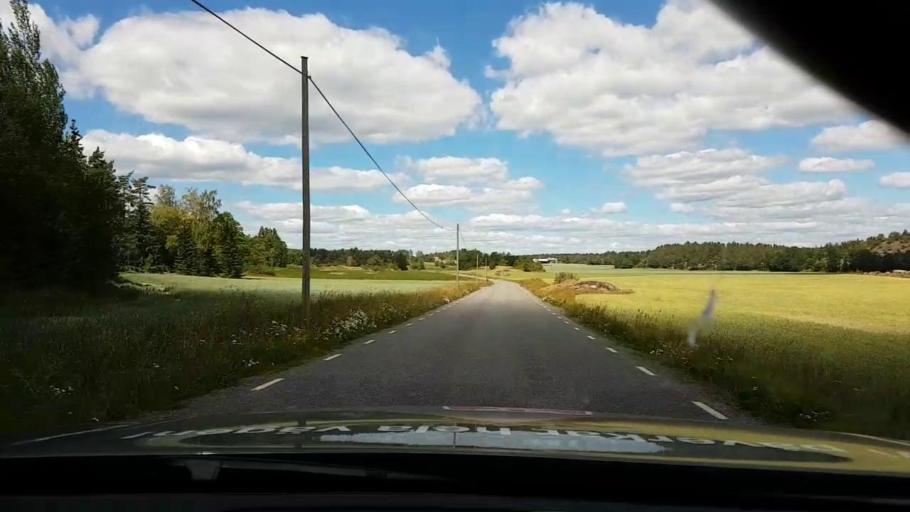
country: SE
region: Kalmar
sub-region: Vasterviks Kommun
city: Forserum
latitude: 58.0011
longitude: 16.5908
